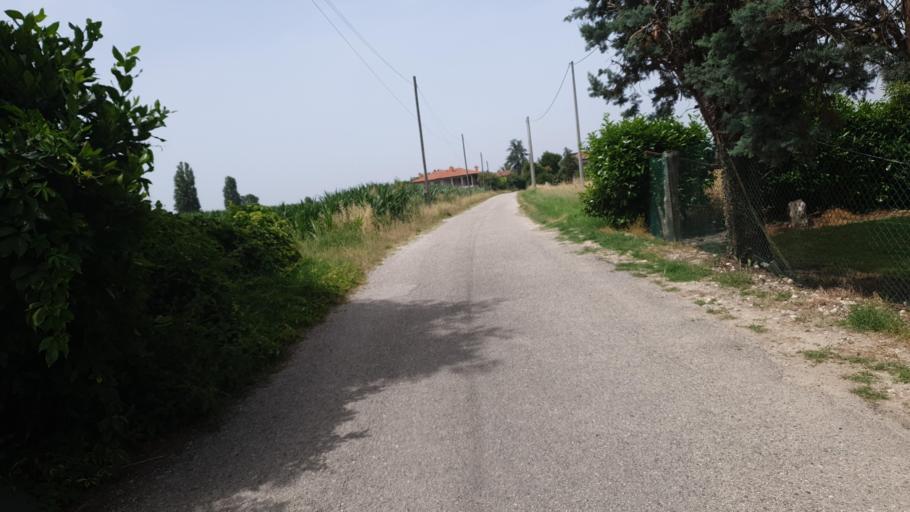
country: IT
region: Veneto
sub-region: Provincia di Padova
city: Polverara
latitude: 45.2902
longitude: 11.9507
